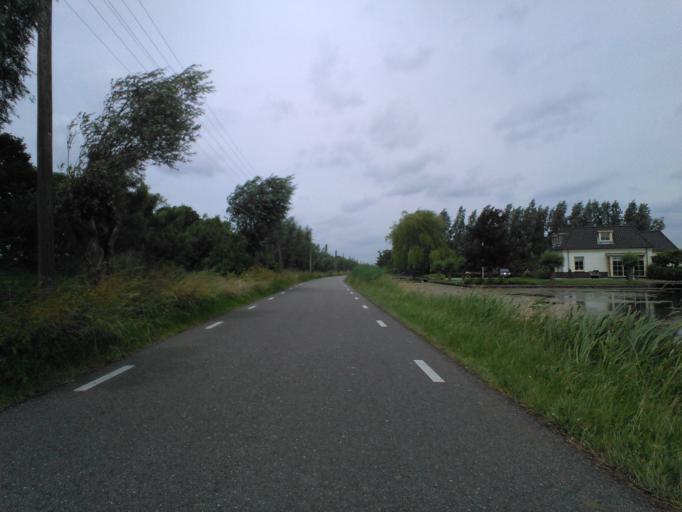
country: NL
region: South Holland
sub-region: Gemeente Vlist
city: Haastrecht
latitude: 51.9824
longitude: 4.7564
